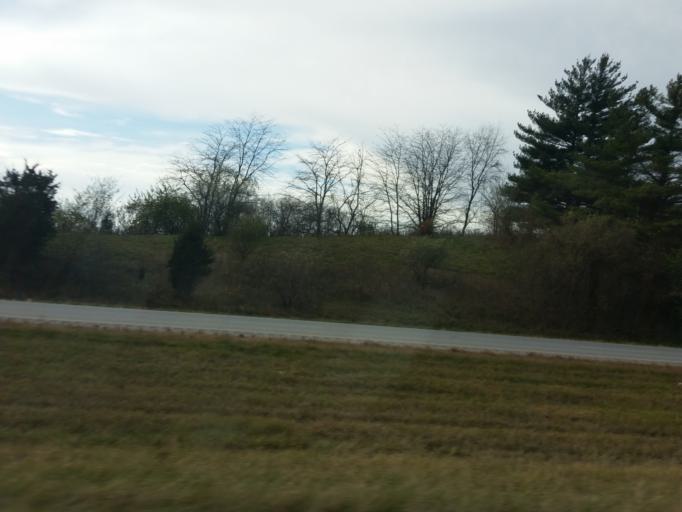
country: US
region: Illinois
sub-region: Henry County
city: Green Rock
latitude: 41.4459
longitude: -90.3663
